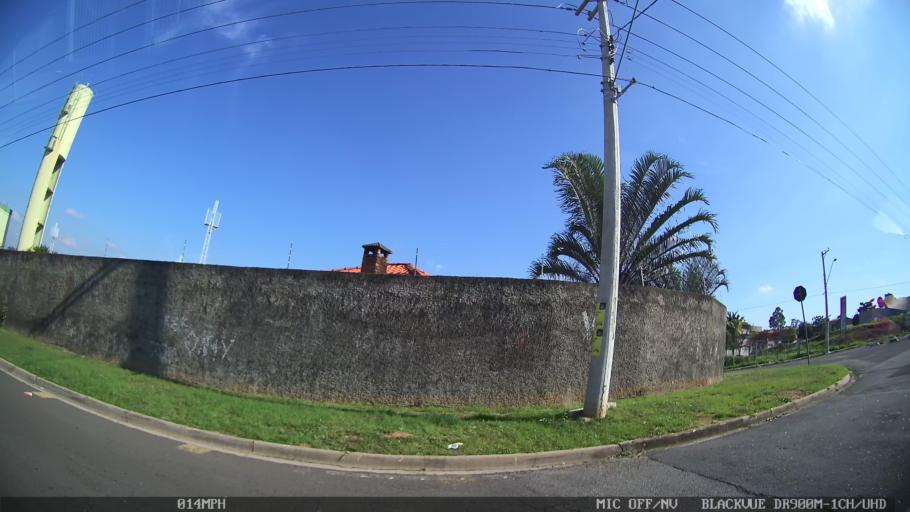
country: BR
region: Sao Paulo
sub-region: Campinas
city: Campinas
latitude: -22.9486
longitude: -47.1197
